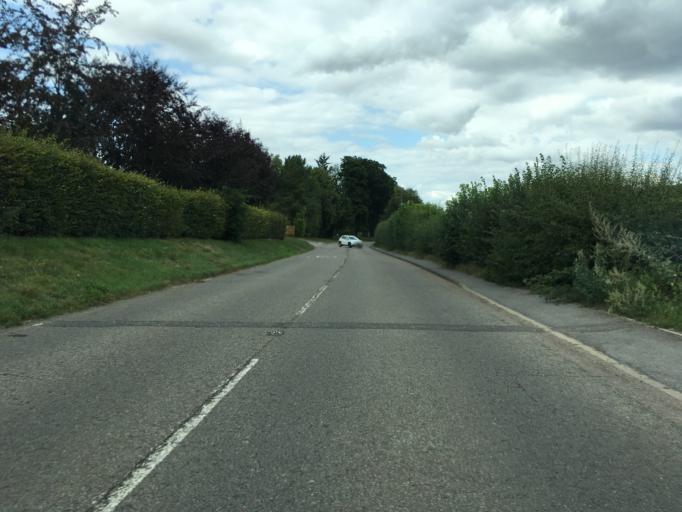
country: GB
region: England
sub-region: West Berkshire
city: Newbury
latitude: 51.4227
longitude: -1.3274
